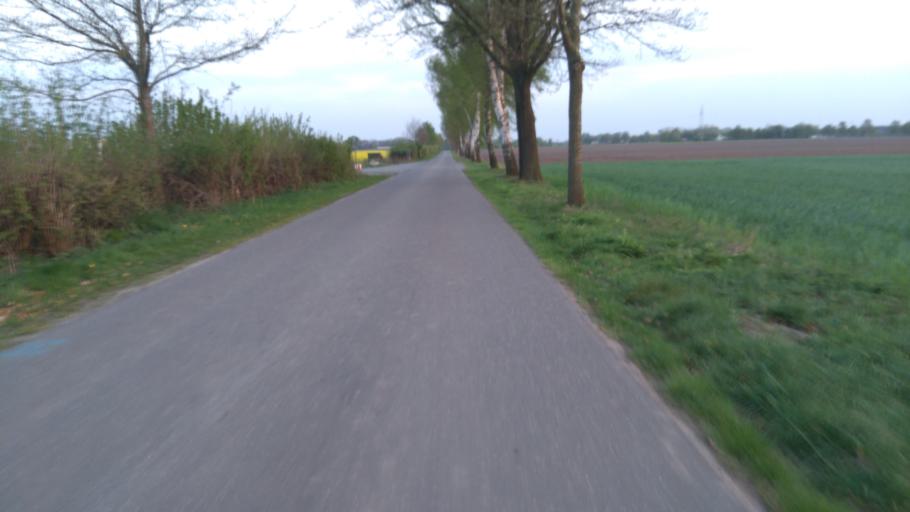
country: DE
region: Lower Saxony
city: Bargstedt
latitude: 53.4787
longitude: 9.4769
